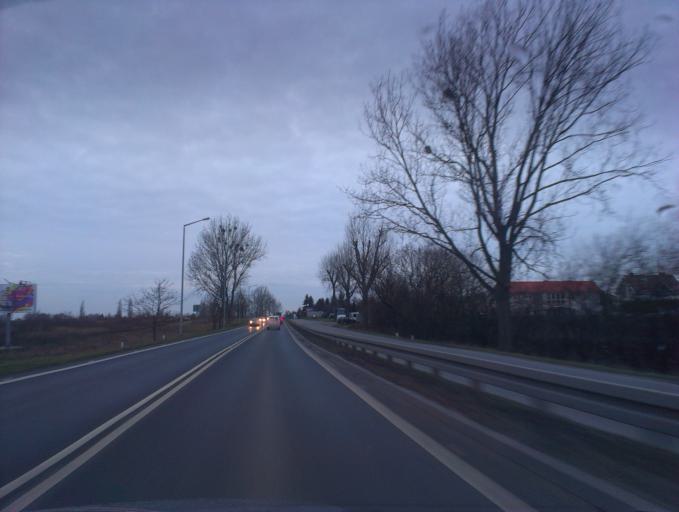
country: PL
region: Greater Poland Voivodeship
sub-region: Powiat poznanski
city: Zlotniki
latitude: 52.4881
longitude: 16.8515
